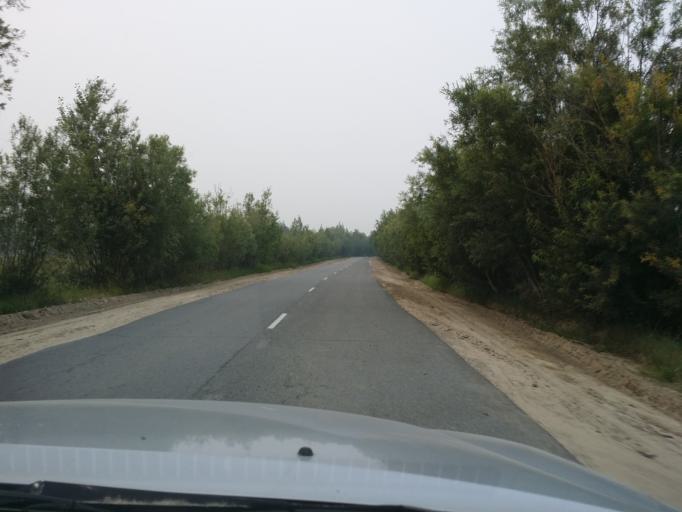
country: RU
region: Khanty-Mansiyskiy Avtonomnyy Okrug
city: Megion
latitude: 61.0008
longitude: 76.3051
